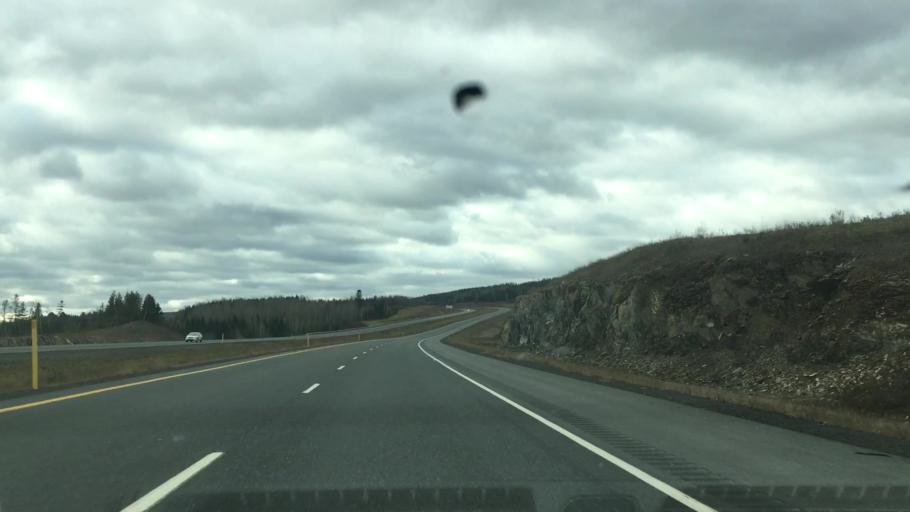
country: US
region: Maine
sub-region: Aroostook County
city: Fort Fairfield
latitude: 46.7349
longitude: -67.7191
